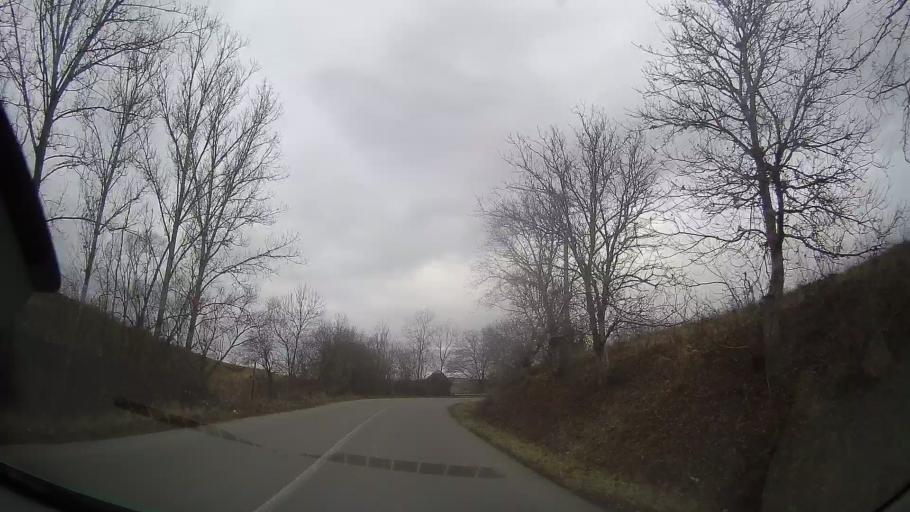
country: RO
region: Mures
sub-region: Comuna Faragau
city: Faragau
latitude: 46.7369
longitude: 24.5405
